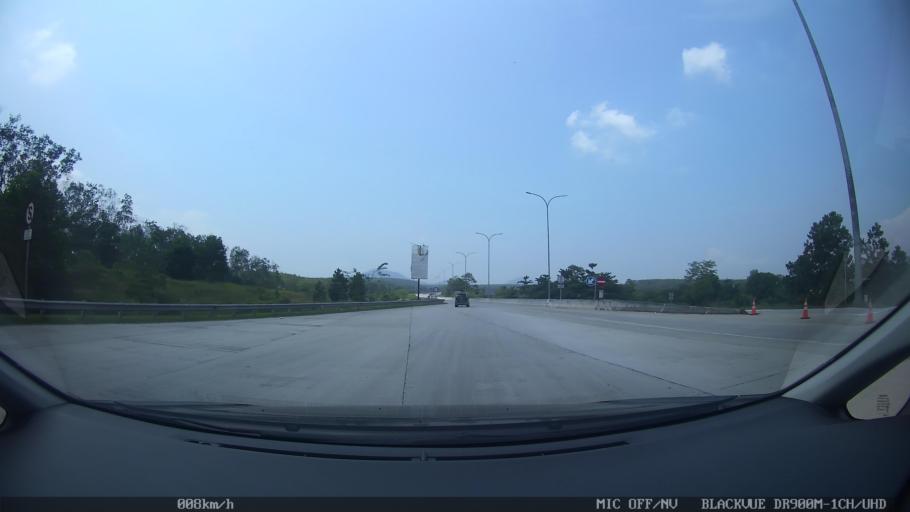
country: ID
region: Lampung
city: Kedaton
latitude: -5.3585
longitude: 105.3276
